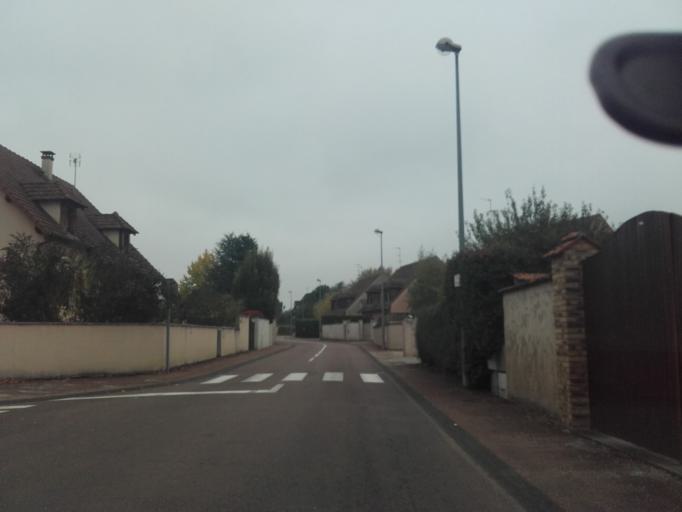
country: FR
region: Bourgogne
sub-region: Departement de la Cote-d'Or
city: Beaune
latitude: 47.0286
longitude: 4.8316
